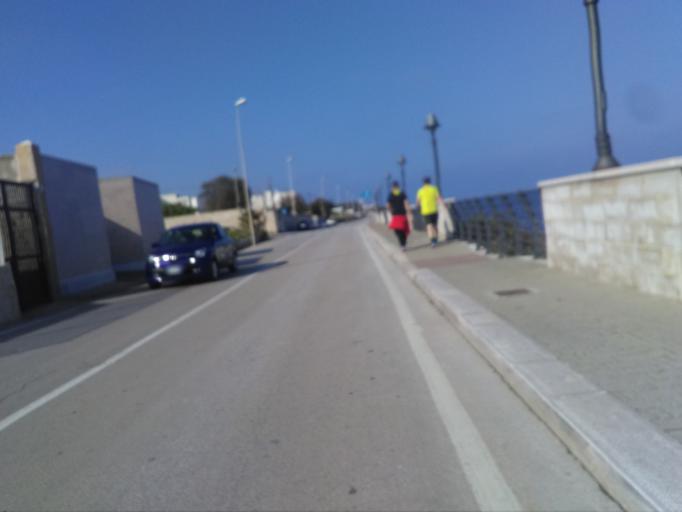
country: IT
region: Apulia
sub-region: Provincia di Bari
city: San Paolo
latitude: 41.1541
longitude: 16.7855
